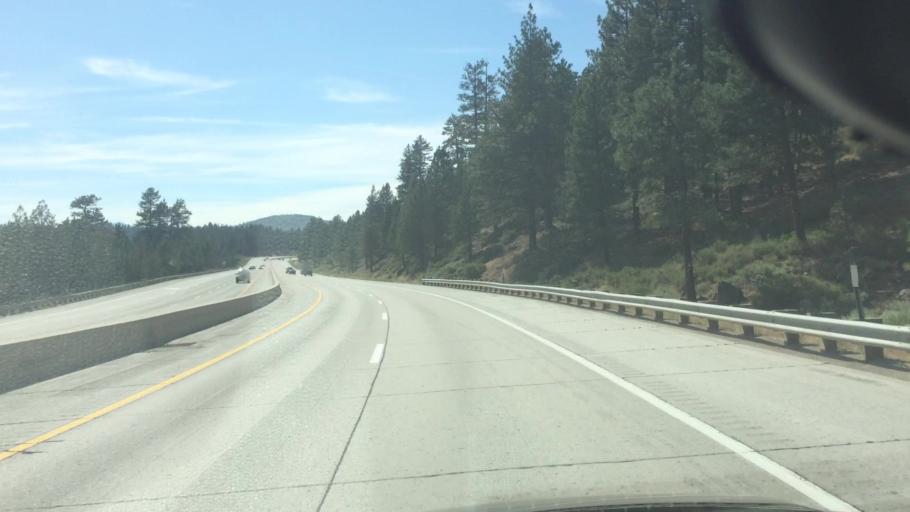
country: US
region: California
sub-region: Placer County
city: Tahoe Vista
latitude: 39.3721
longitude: -120.0529
